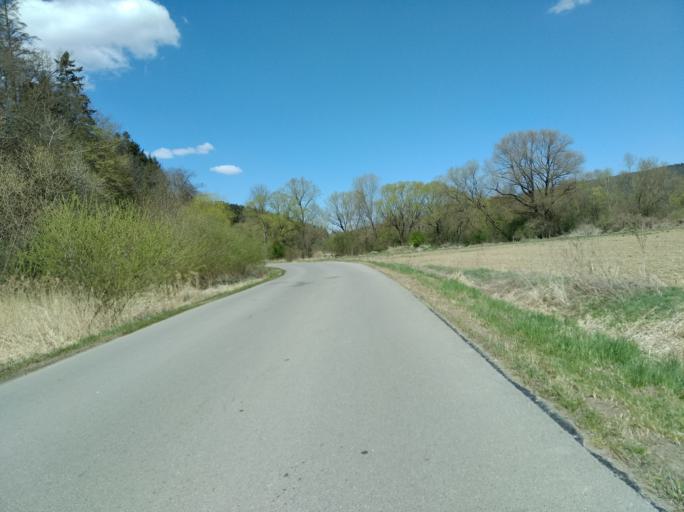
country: PL
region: Subcarpathian Voivodeship
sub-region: Powiat brzozowski
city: Dydnia
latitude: 49.6821
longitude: 22.2421
